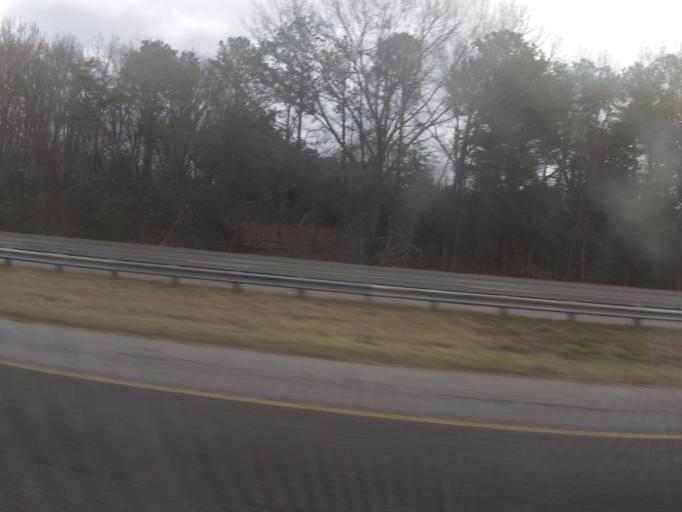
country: US
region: Georgia
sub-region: Whitfield County
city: Dalton
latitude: 34.7661
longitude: -85.0018
